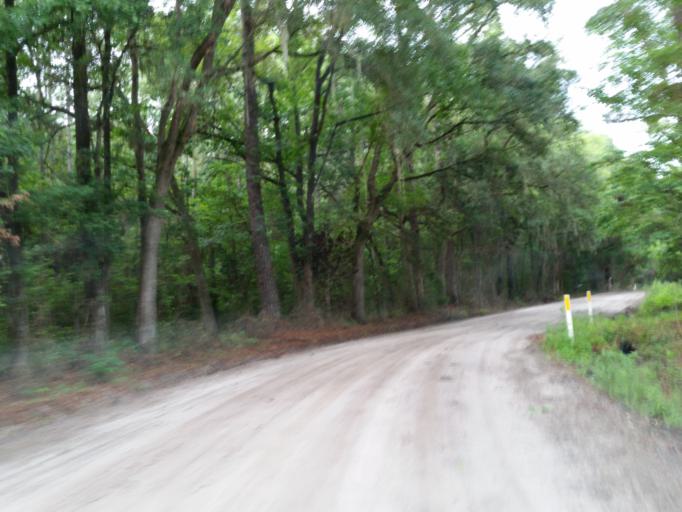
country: US
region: Florida
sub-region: Alachua County
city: High Springs
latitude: 29.9695
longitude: -82.5654
